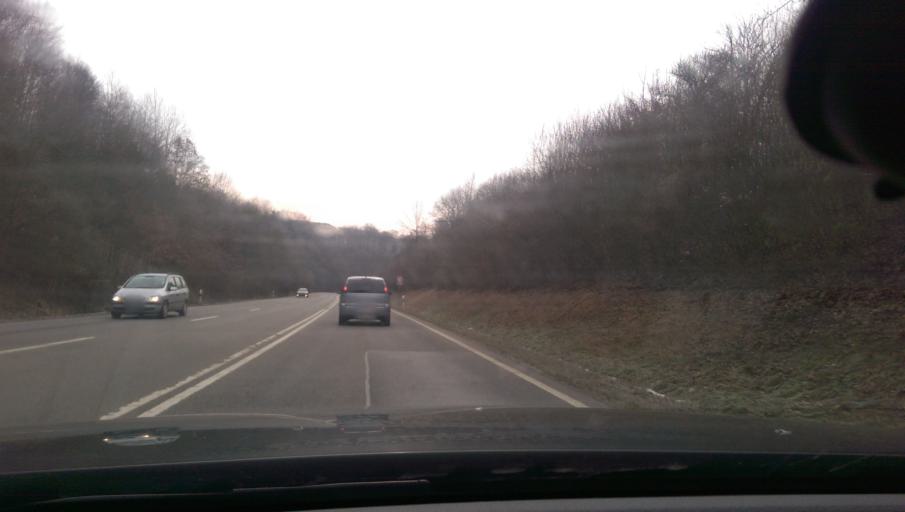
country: DE
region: Bavaria
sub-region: Lower Bavaria
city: Passau
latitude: 48.5807
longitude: 13.4222
